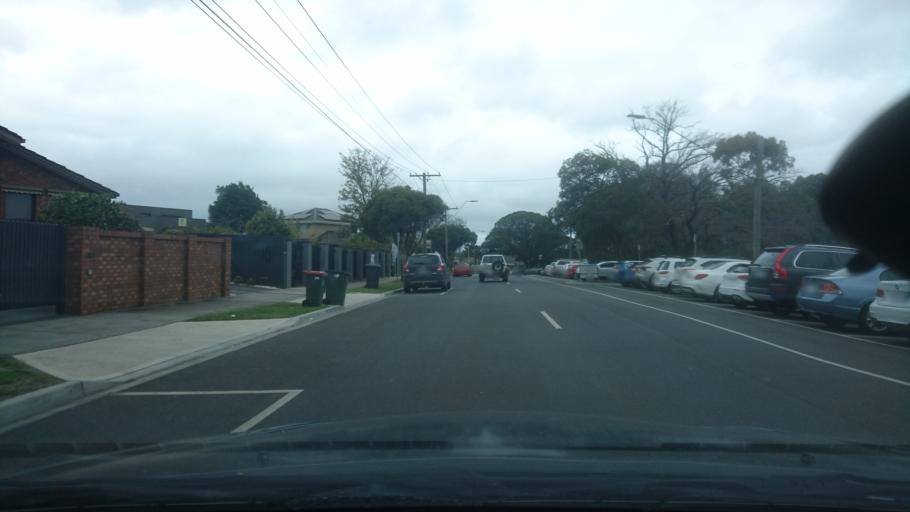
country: AU
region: Victoria
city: Murrumbeena
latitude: -37.9054
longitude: 145.0656
